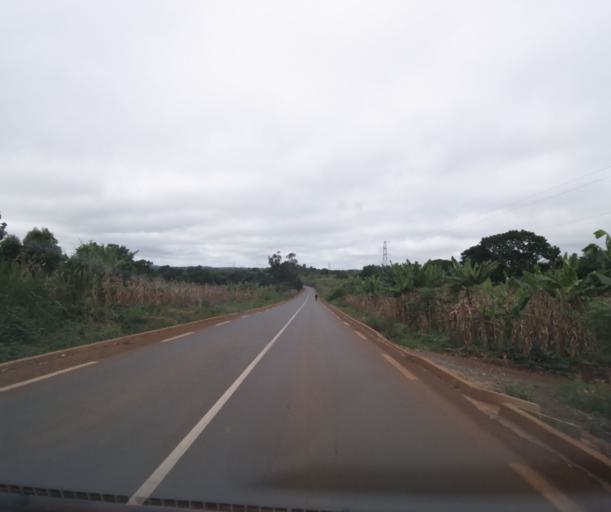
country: CM
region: West
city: Bansoa
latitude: 5.5431
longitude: 10.3282
